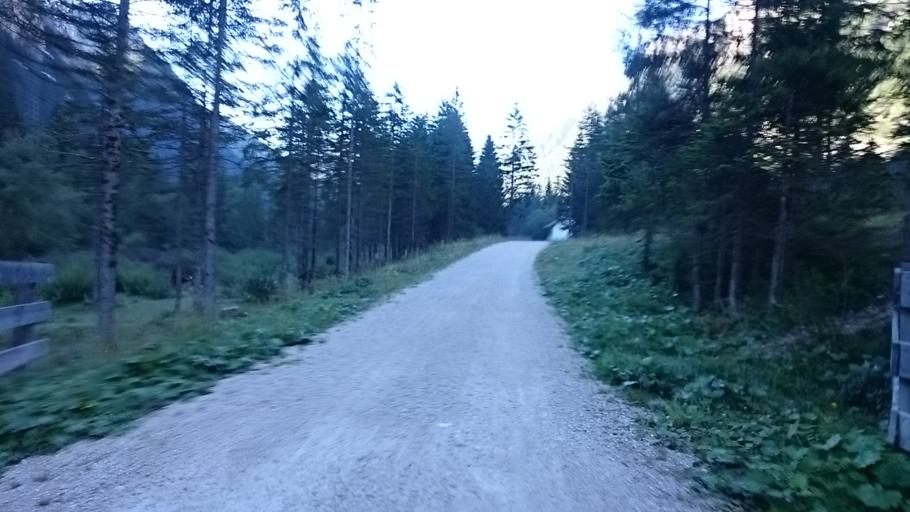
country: IT
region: Trentino-Alto Adige
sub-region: Bolzano
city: Dobbiaco
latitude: 46.6710
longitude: 12.2216
